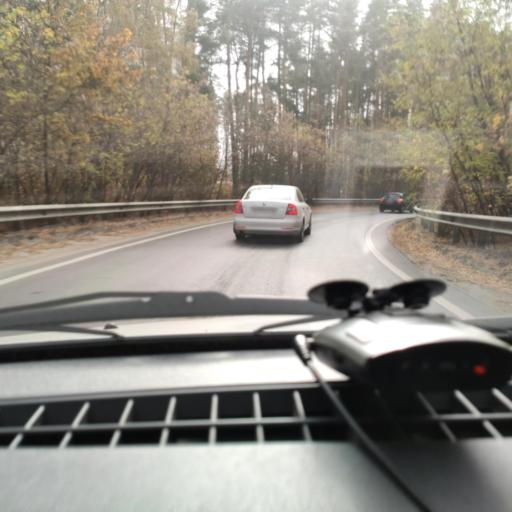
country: RU
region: Voronezj
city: Podgornoye
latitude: 51.7347
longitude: 39.1827
